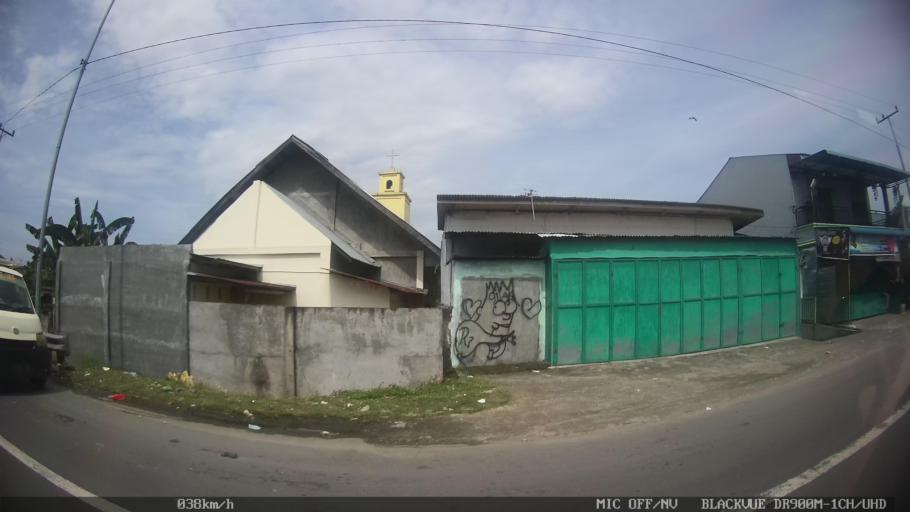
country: ID
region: North Sumatra
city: Sunggal
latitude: 3.6161
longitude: 98.6286
